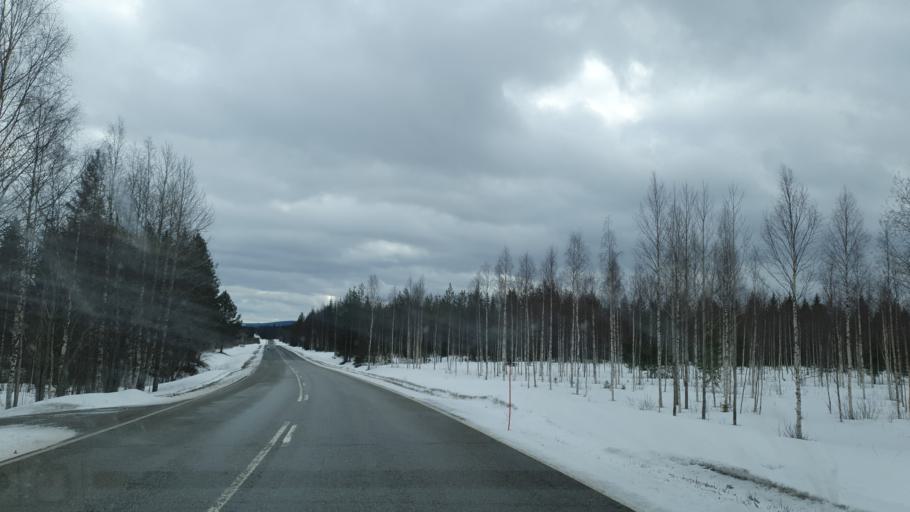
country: FI
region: Kainuu
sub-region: Kehys-Kainuu
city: Puolanka
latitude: 65.2149
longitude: 27.6002
